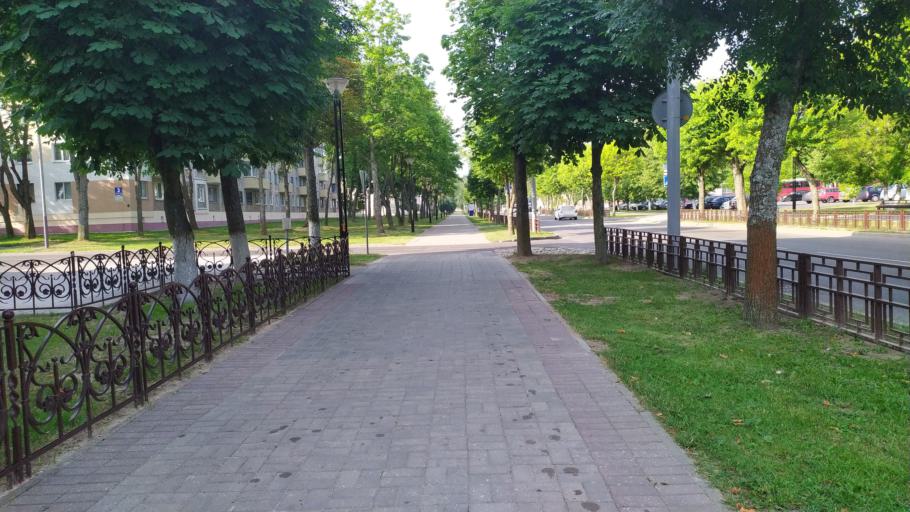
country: BY
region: Vitebsk
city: Navapolatsk
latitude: 55.5337
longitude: 28.6477
